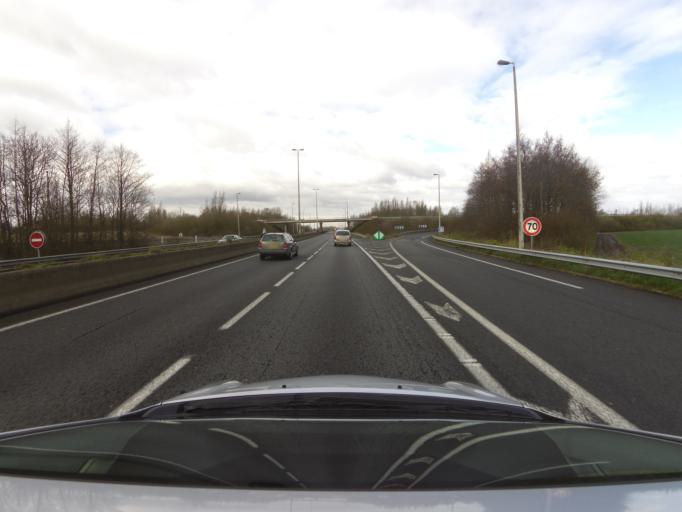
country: FR
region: Nord-Pas-de-Calais
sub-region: Departement du Pas-de-Calais
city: Marck
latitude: 50.9360
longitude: 1.9726
